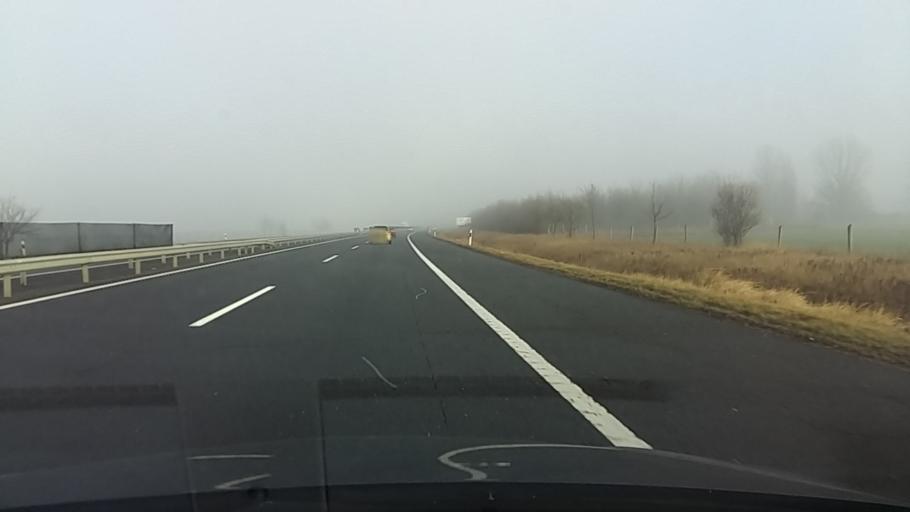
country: HU
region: Borsod-Abauj-Zemplen
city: Mezokeresztes
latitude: 47.8602
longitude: 20.7592
